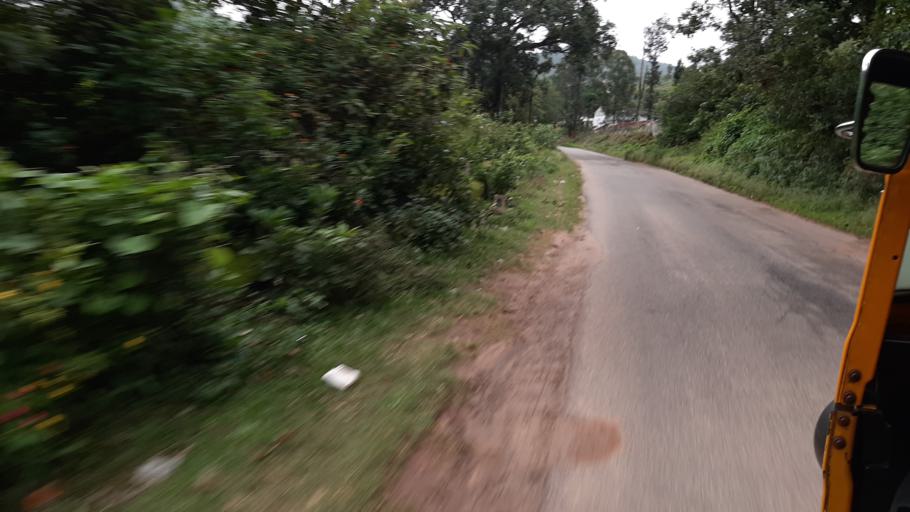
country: IN
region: Andhra Pradesh
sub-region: Vizianagaram District
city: Salur
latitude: 18.2372
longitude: 83.0030
